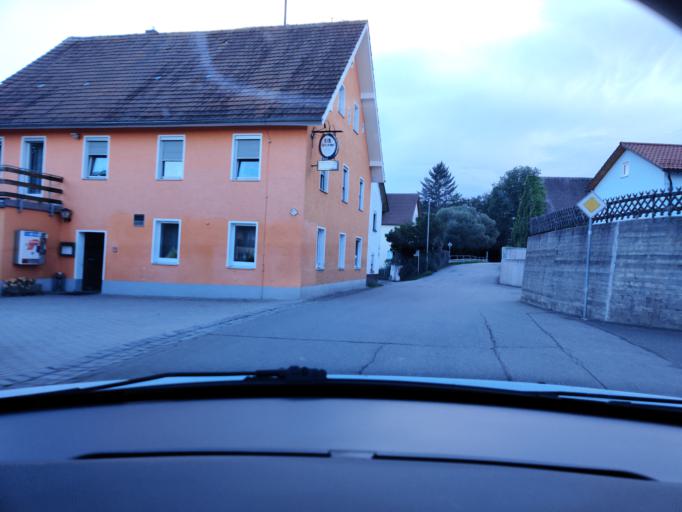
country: DE
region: Bavaria
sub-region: Upper Palatinate
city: Pfreimd
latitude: 49.4865
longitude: 12.1661
